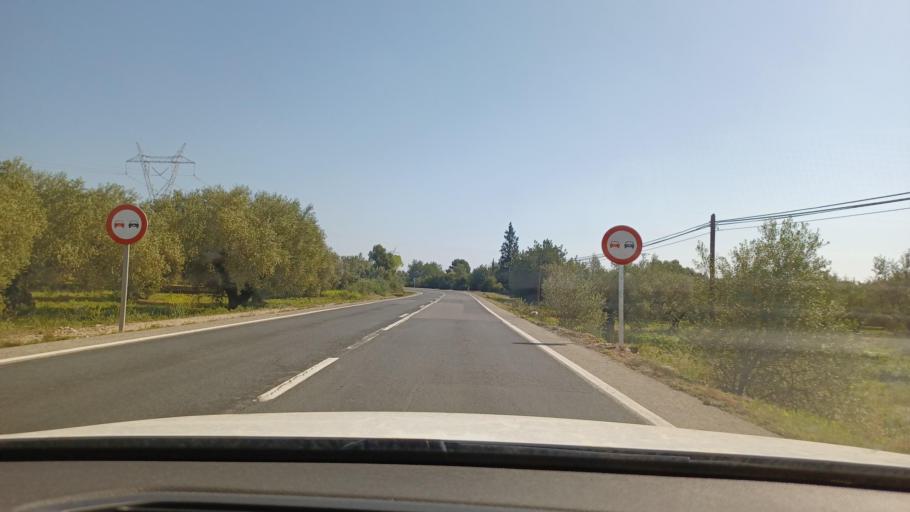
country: ES
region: Catalonia
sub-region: Provincia de Tarragona
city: Santa Barbara
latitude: 40.6902
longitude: 0.4728
